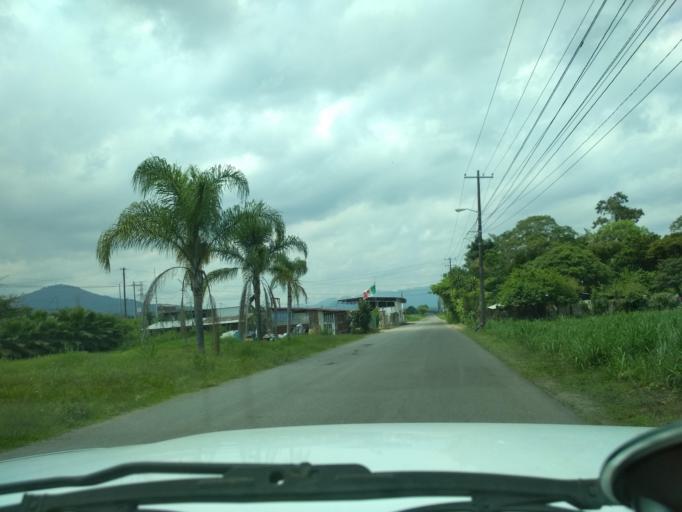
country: MX
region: Veracruz
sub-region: Ixtaczoquitlan
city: Buenavista
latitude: 18.8874
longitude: -97.0471
